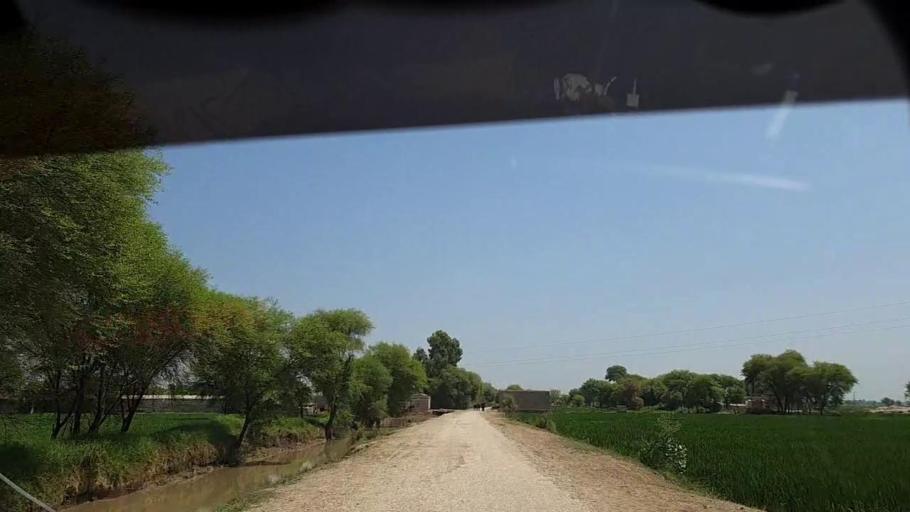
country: PK
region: Sindh
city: Ghauspur
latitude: 28.1700
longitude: 69.0662
